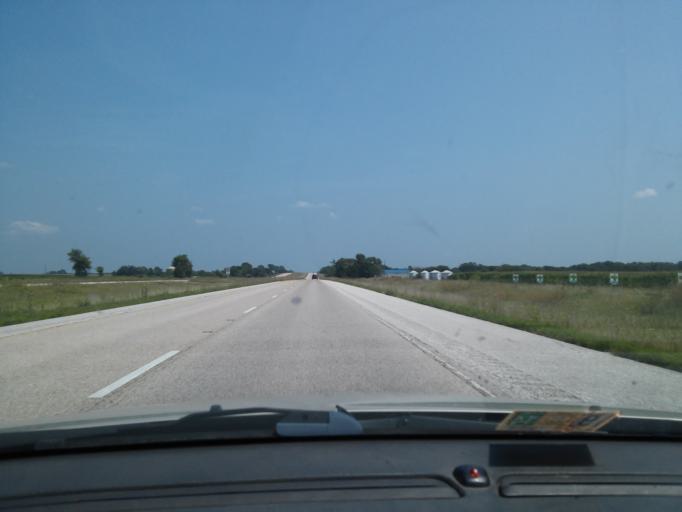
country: US
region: Illinois
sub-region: Scott County
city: Winchester
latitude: 39.6812
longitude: -90.4440
